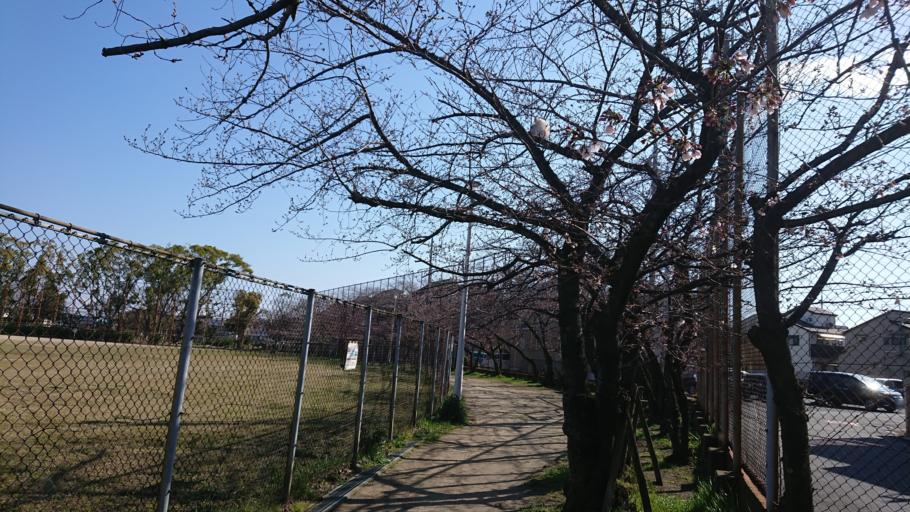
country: JP
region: Osaka
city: Takaishi
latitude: 34.5041
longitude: 135.4196
